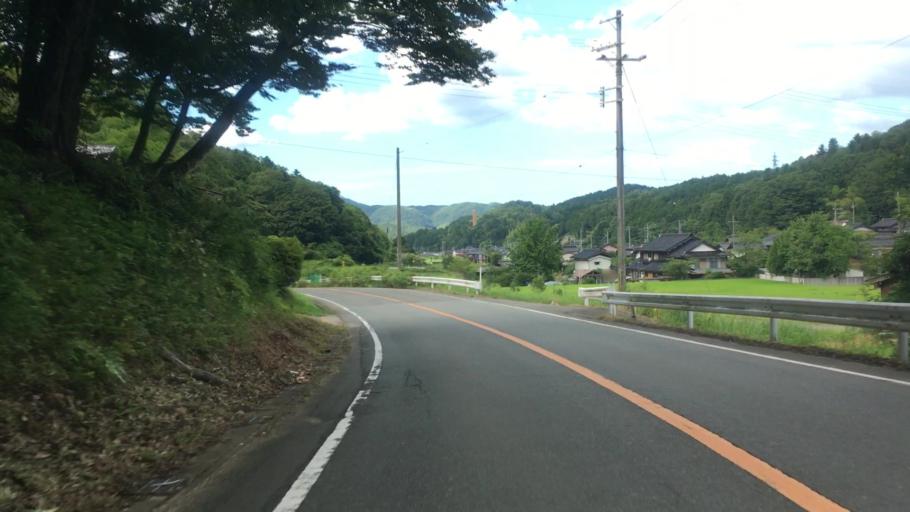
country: JP
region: Hyogo
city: Toyooka
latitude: 35.5328
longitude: 134.7886
